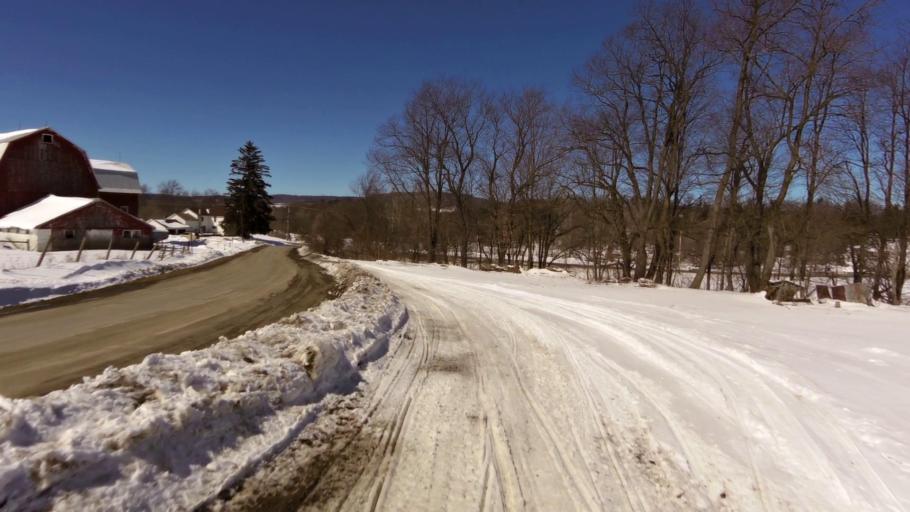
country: US
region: New York
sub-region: Allegany County
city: Houghton
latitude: 42.3809
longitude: -78.2538
